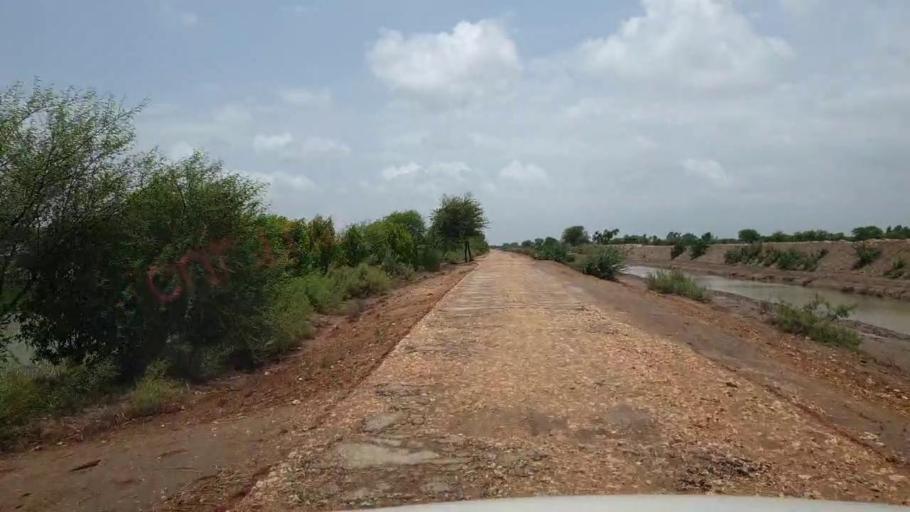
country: PK
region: Sindh
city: Kario
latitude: 24.7130
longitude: 68.5920
